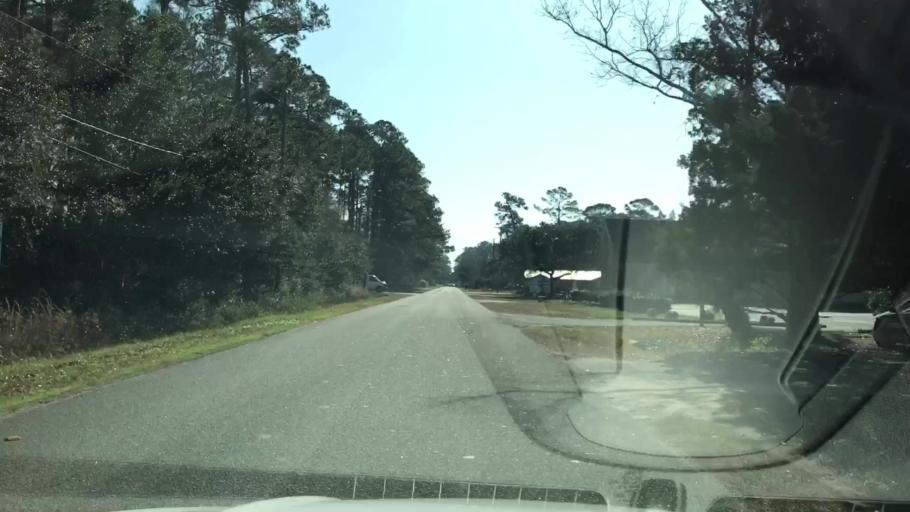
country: US
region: South Carolina
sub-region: Horry County
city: Garden City
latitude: 33.5872
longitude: -79.0056
